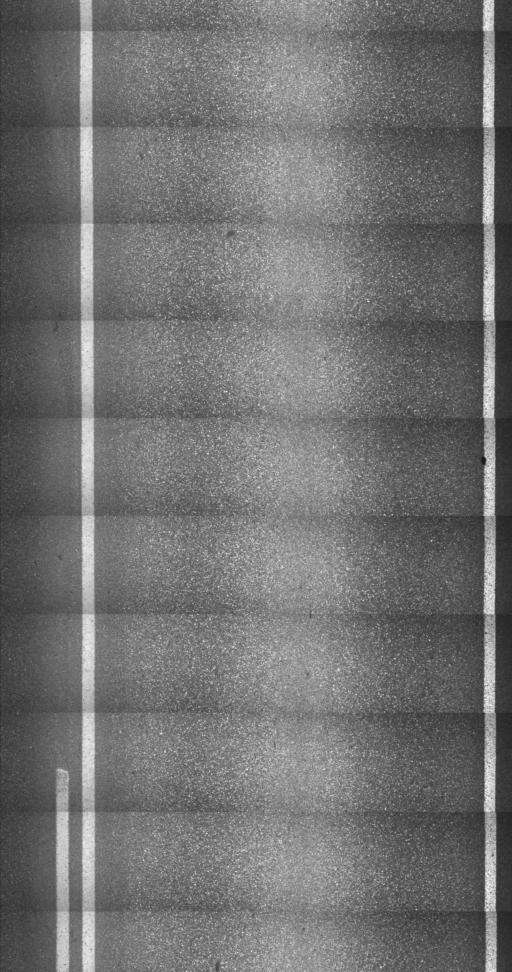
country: US
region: Vermont
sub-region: Chittenden County
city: Colchester
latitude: 44.5825
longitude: -73.1635
